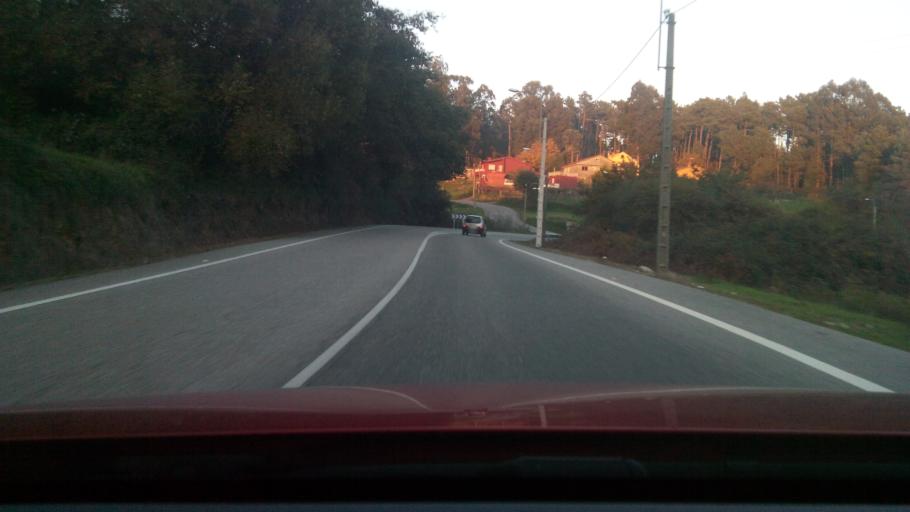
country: ES
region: Galicia
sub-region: Provincia de Pontevedra
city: Gondomar
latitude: 42.1585
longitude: -8.7075
